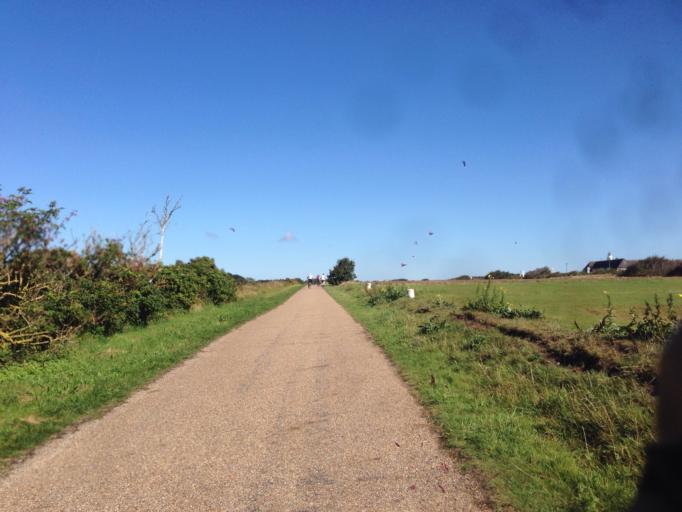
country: DE
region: Schleswig-Holstein
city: Tinnum
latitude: 54.9397
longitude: 8.3310
